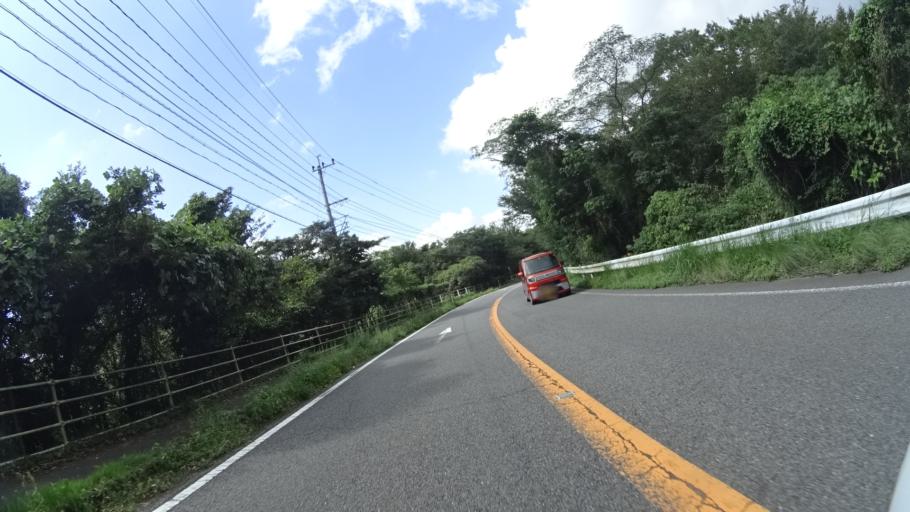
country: JP
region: Oita
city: Beppu
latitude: 33.3503
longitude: 131.4422
